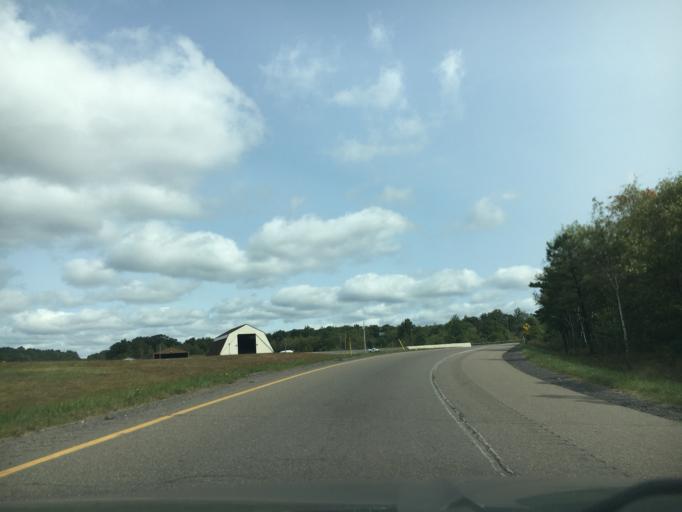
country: US
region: Pennsylvania
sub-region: Schuylkill County
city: McAdoo
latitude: 40.8794
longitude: -76.0021
